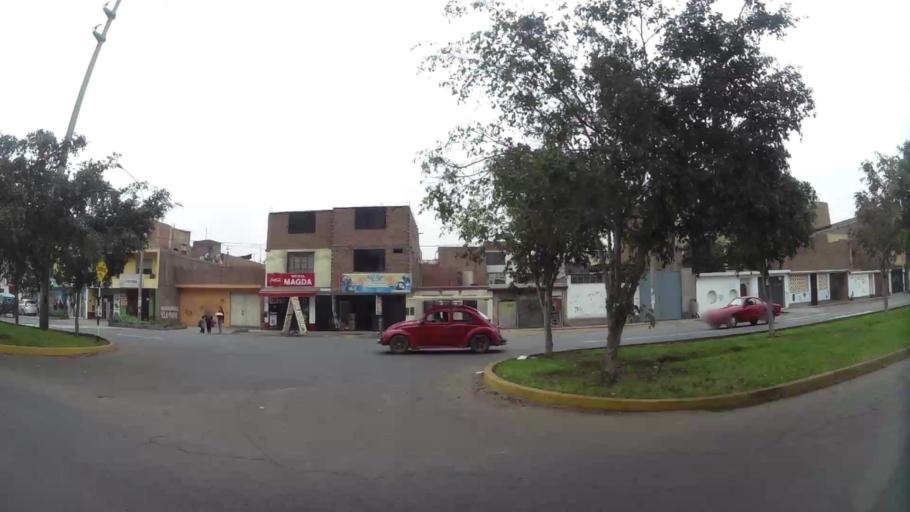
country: PE
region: Lima
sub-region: Lima
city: Independencia
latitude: -11.9420
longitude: -77.0780
